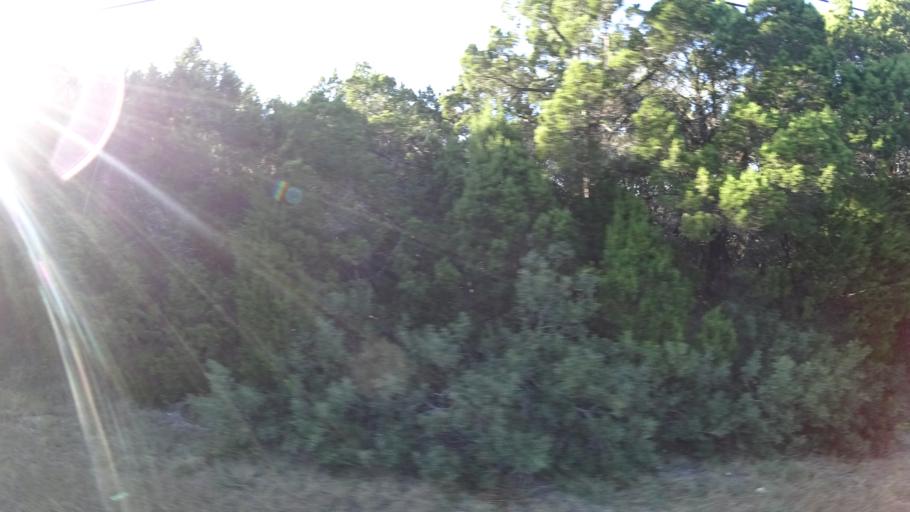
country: US
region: Texas
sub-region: Travis County
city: Barton Creek
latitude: 30.2491
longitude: -97.8492
